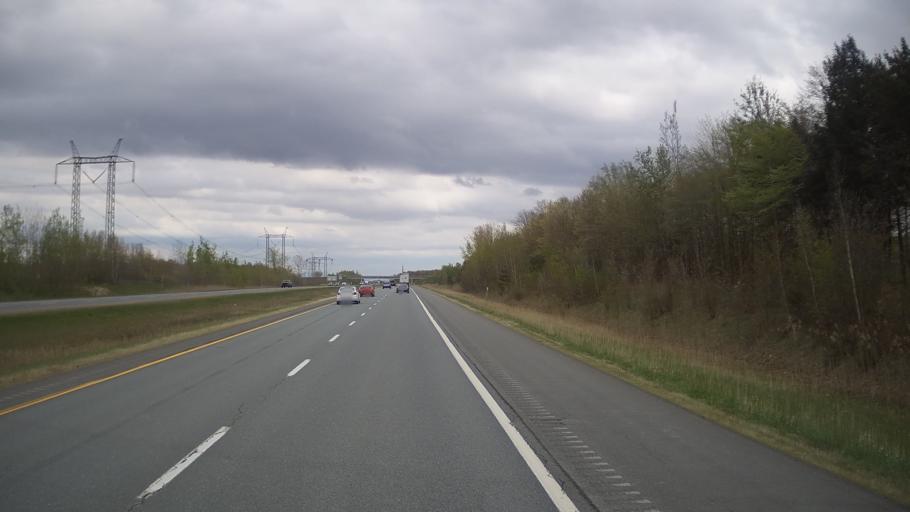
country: CA
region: Quebec
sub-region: Monteregie
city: Rougemont
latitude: 45.4001
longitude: -73.0903
